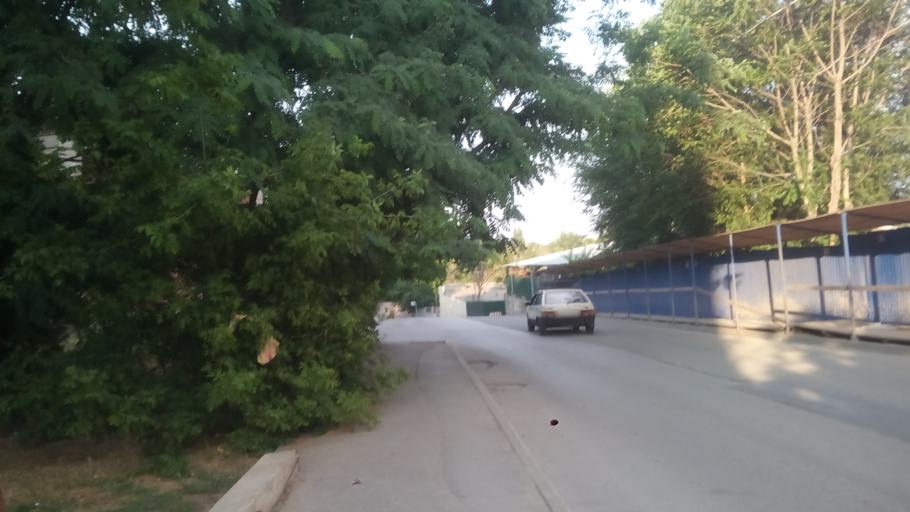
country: RU
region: Rostov
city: Imeni Chkalova
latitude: 47.2581
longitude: 39.7742
